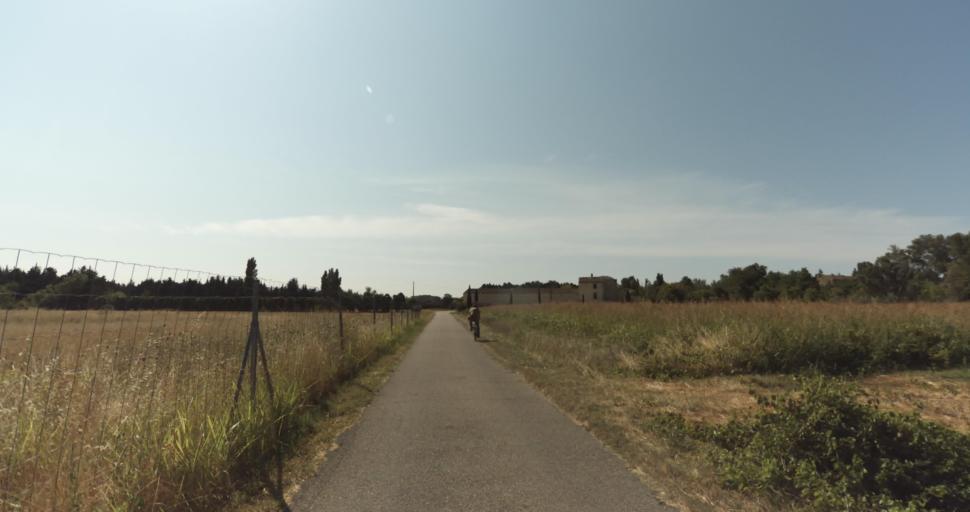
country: FR
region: Provence-Alpes-Cote d'Azur
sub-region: Departement du Vaucluse
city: Althen-des-Paluds
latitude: 44.0133
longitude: 4.9629
